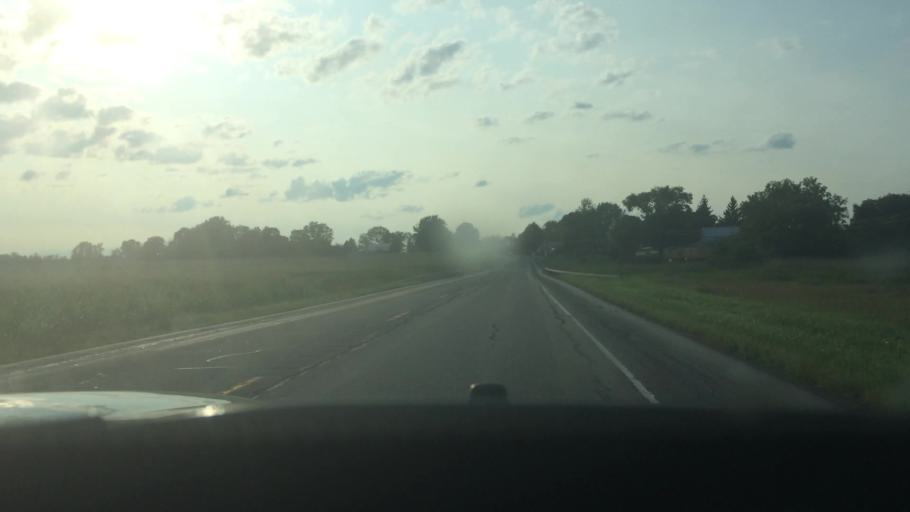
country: US
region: New York
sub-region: St. Lawrence County
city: Ogdensburg
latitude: 44.6697
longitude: -75.3801
